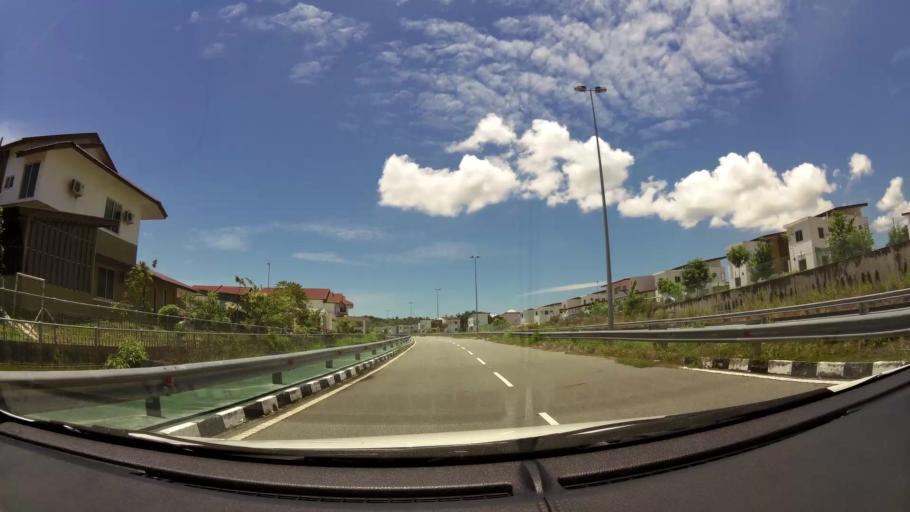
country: BN
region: Brunei and Muara
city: Bandar Seri Begawan
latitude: 5.0073
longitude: 115.0041
